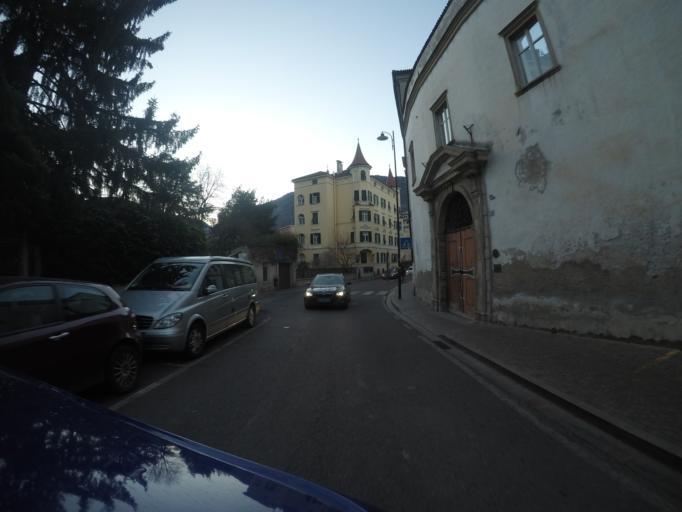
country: IT
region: Trentino-Alto Adige
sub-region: Bolzano
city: Bolzano
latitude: 46.5030
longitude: 11.3567
